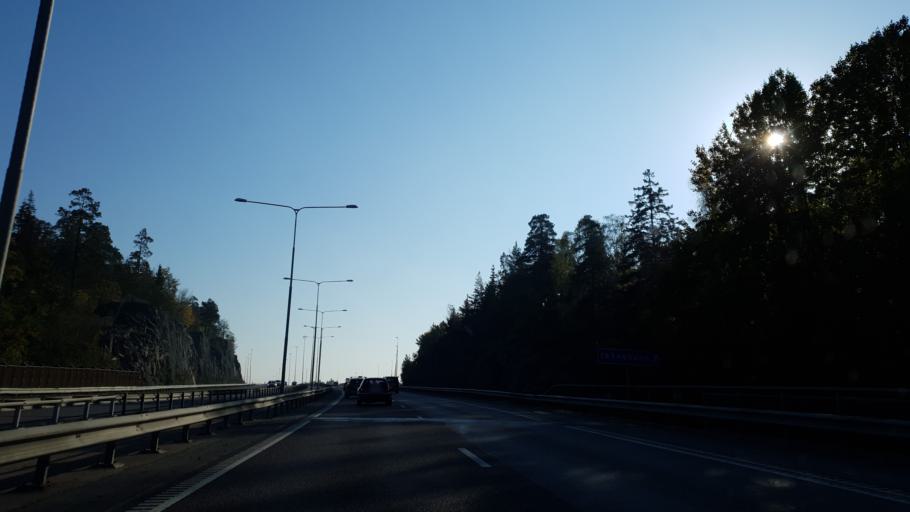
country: SE
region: Stockholm
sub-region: Haninge Kommun
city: Handen
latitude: 59.2344
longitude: 18.1230
